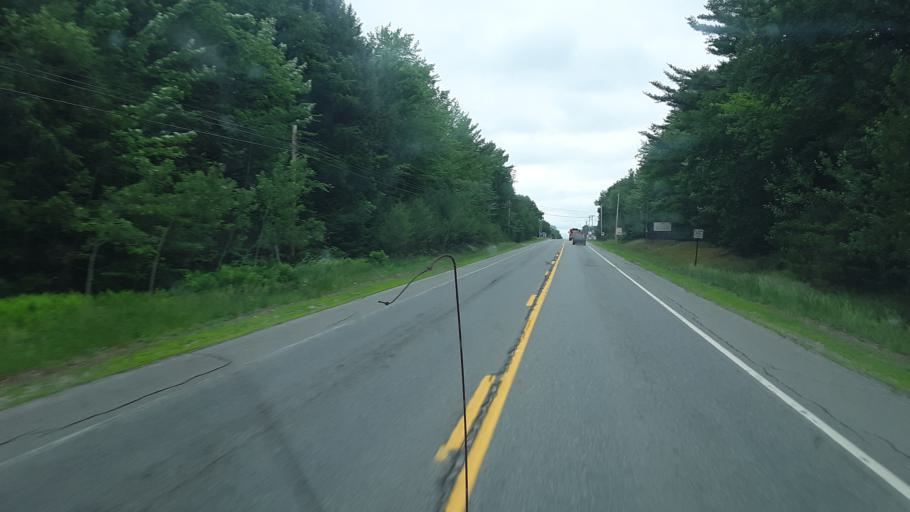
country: US
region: Maine
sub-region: Penobscot County
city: Millinocket
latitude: 45.6570
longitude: -68.6741
